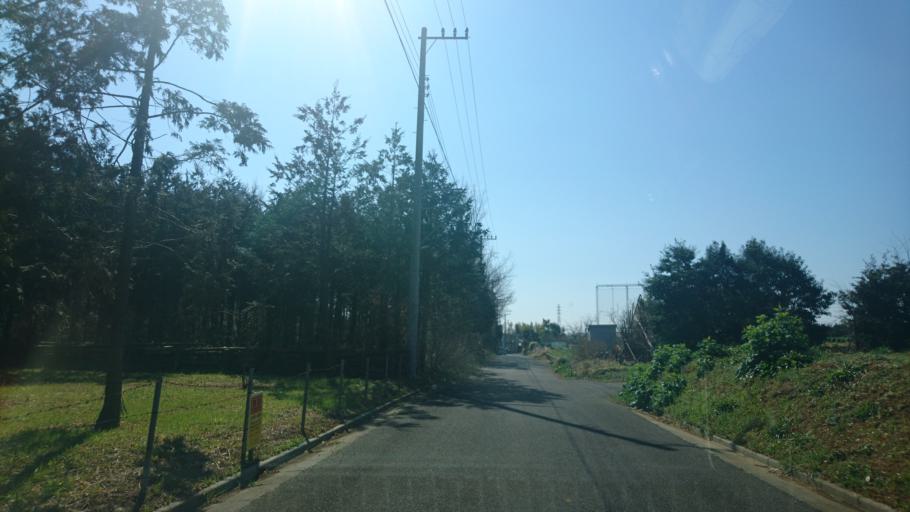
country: JP
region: Kanagawa
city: Fujisawa
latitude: 35.3968
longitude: 139.4374
